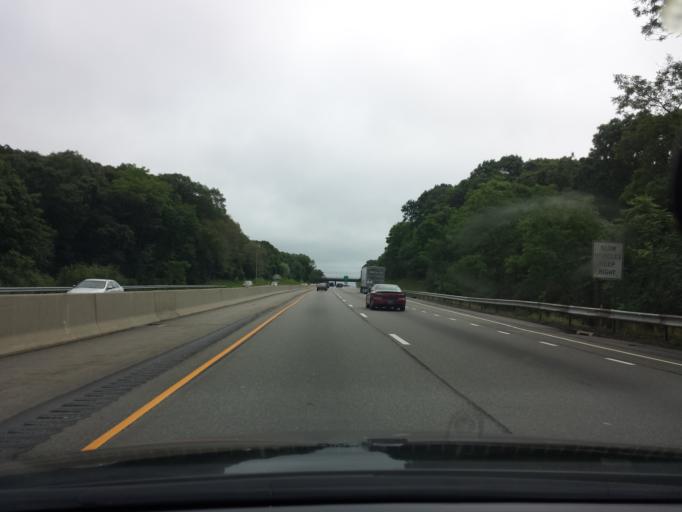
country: US
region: Connecticut
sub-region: Middlesex County
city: Clinton
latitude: 41.2889
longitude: -72.5196
